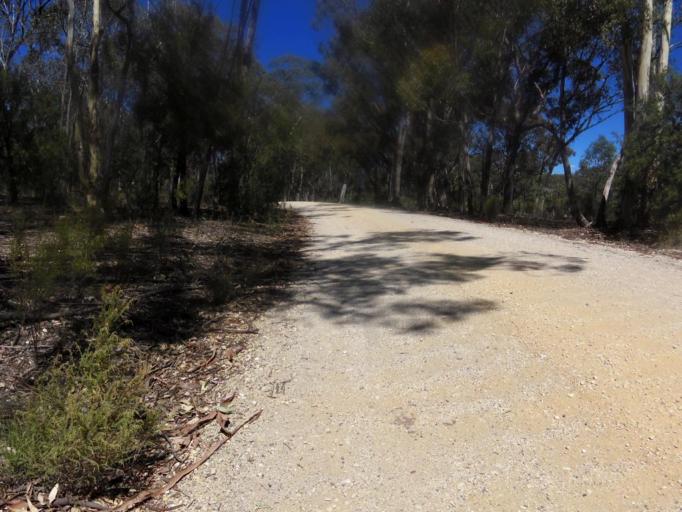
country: AU
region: Victoria
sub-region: Mount Alexander
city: Castlemaine
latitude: -37.0476
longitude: 144.1815
